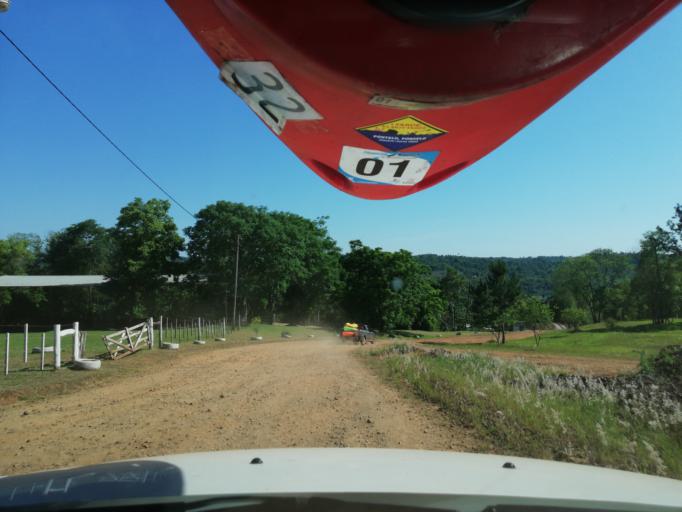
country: AR
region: Misiones
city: Puerto Leoni
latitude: -26.9611
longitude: -55.1527
